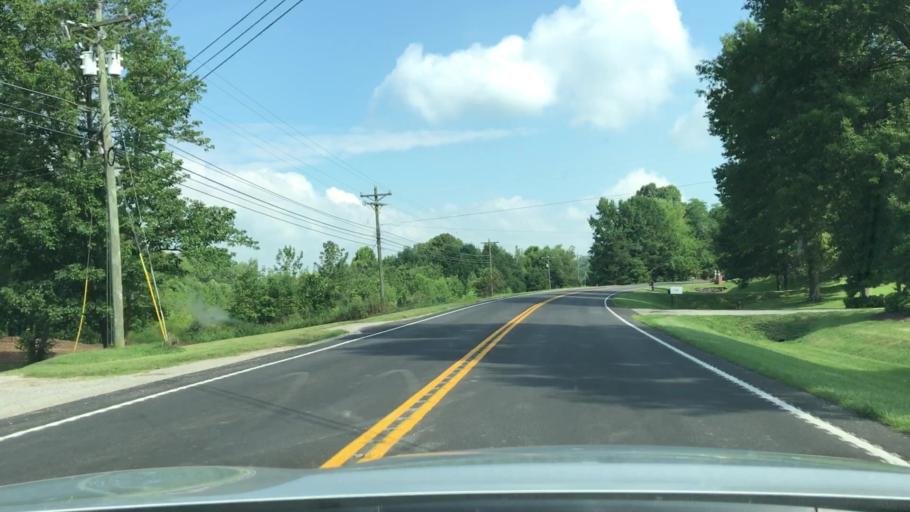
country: US
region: Kentucky
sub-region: Barren County
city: Glasgow
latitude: 37.0276
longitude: -85.9075
